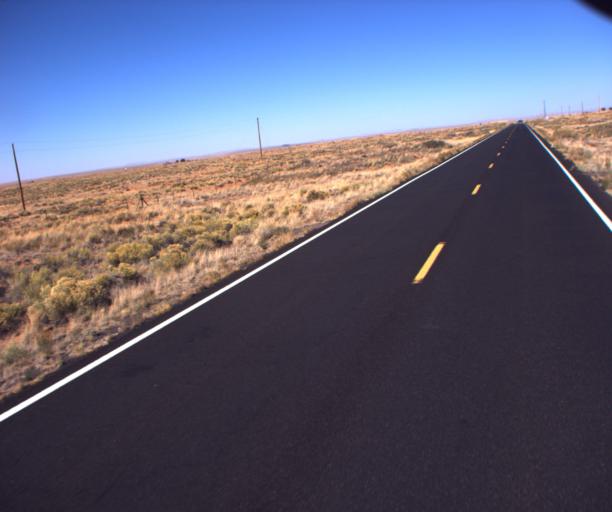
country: US
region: Arizona
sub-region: Navajo County
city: Dilkon
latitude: 35.4989
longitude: -110.4339
